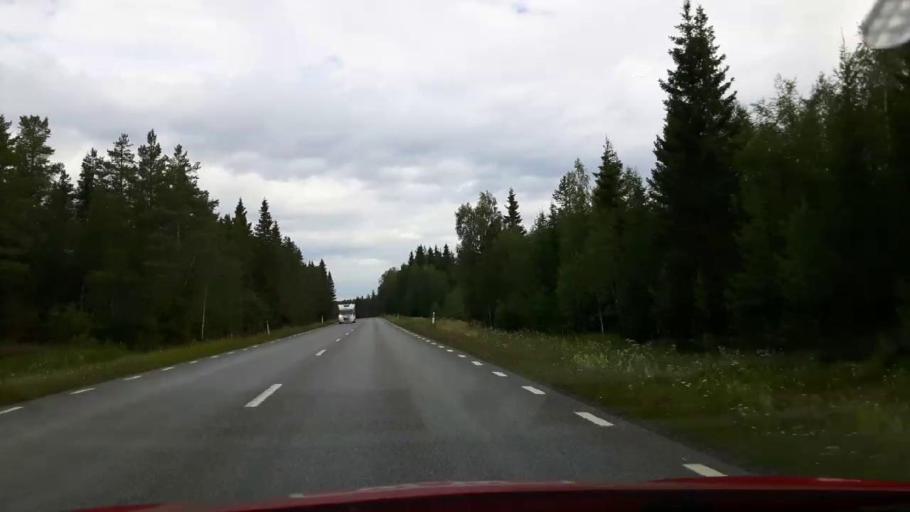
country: SE
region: Jaemtland
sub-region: Stroemsunds Kommun
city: Stroemsund
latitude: 63.5516
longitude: 15.3728
